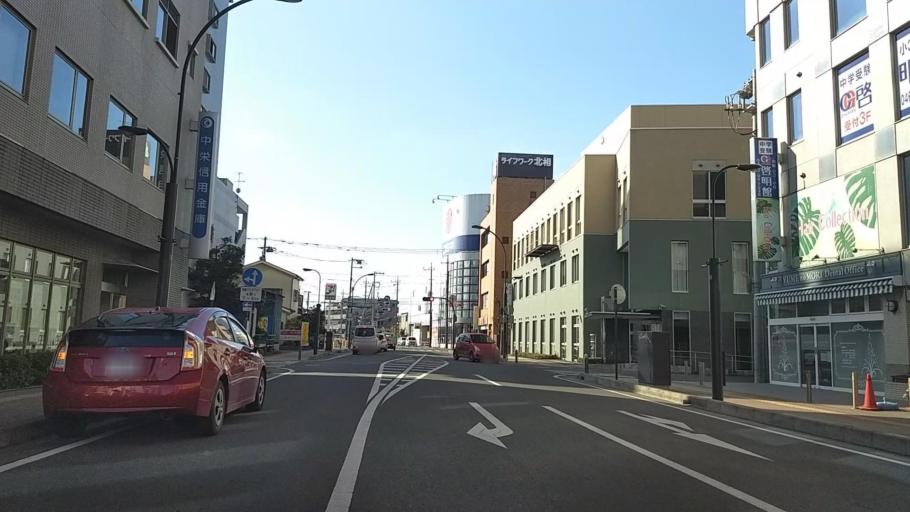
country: JP
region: Kanagawa
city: Isehara
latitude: 35.3949
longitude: 139.3137
